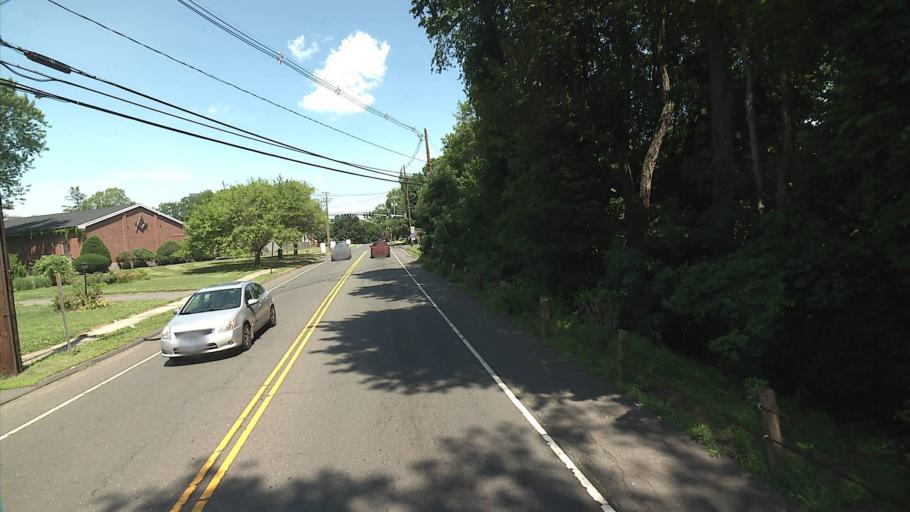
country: US
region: Connecticut
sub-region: Hartford County
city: New Britain
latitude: 41.6525
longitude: -72.7953
